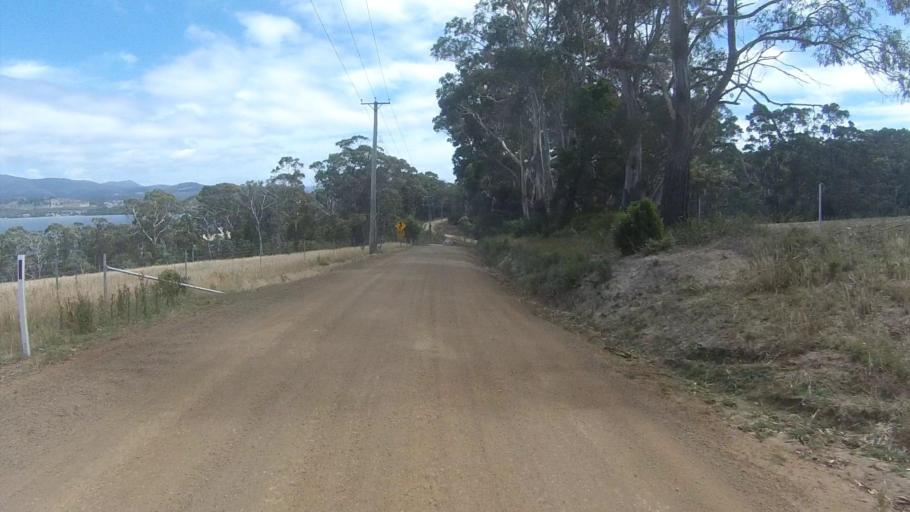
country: AU
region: Tasmania
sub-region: Kingborough
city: Blackmans Bay
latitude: -43.0518
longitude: 147.3113
